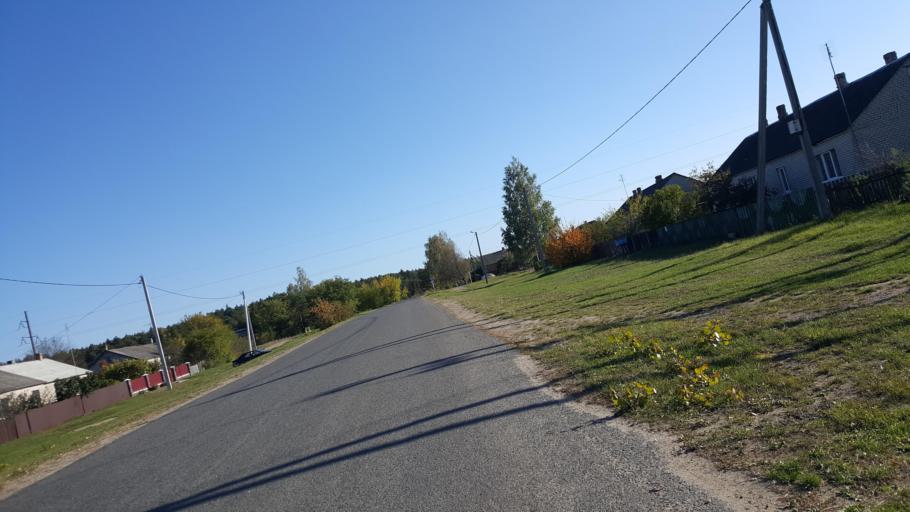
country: BY
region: Brest
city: Kamyanyets
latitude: 52.4143
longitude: 23.8887
